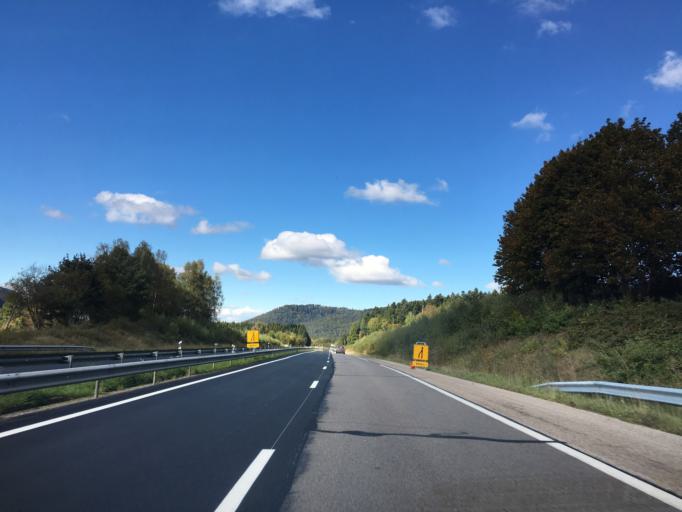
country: FR
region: Lorraine
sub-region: Departement des Vosges
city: Moyenmoutier
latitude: 48.3633
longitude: 6.8849
